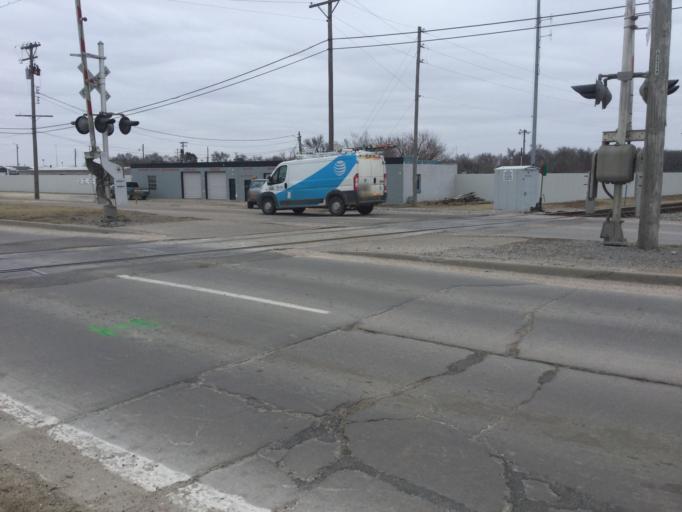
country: US
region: Kansas
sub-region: Sedgwick County
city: Haysville
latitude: 37.6227
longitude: -97.3364
